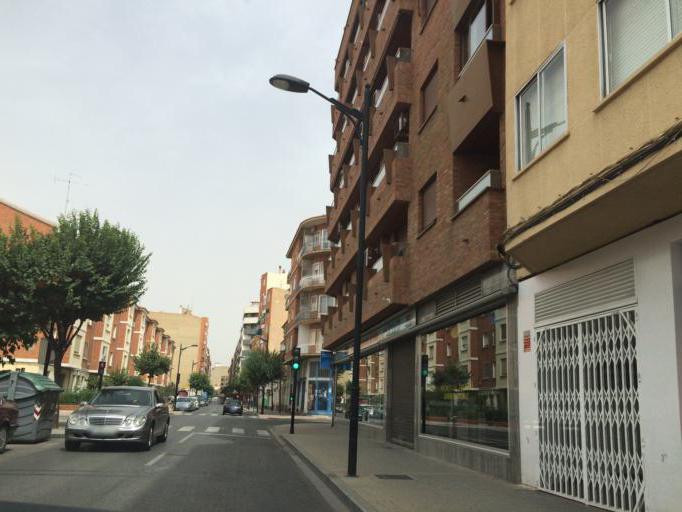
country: ES
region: Castille-La Mancha
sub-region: Provincia de Albacete
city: Albacete
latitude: 38.9860
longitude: -1.8624
